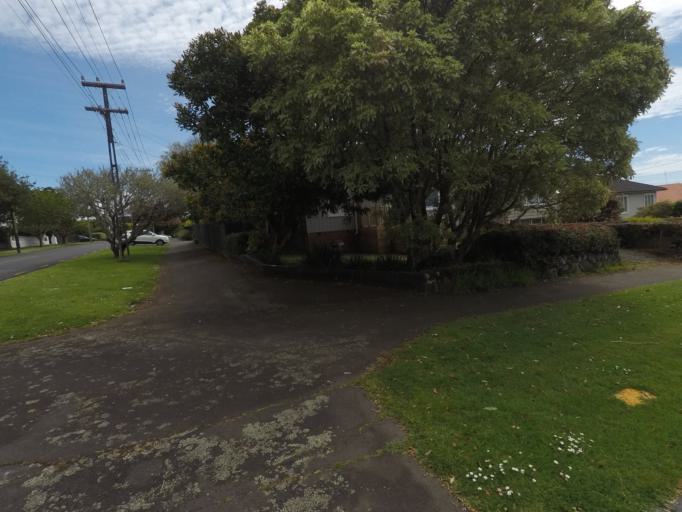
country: NZ
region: Auckland
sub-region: Auckland
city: Auckland
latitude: -36.8852
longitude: 174.7211
